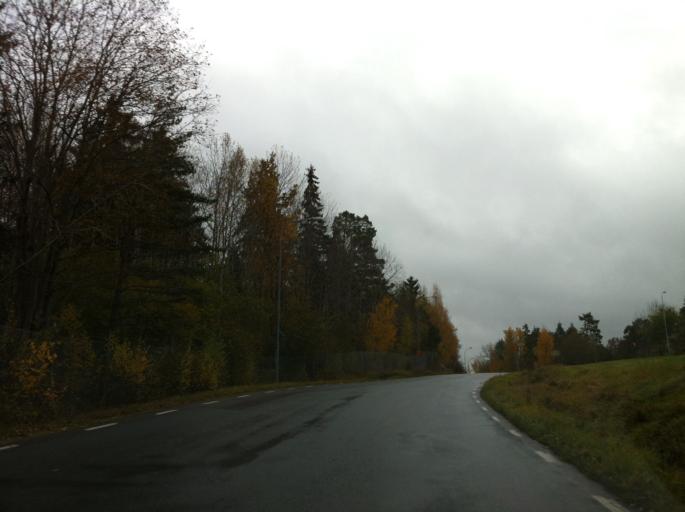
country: SE
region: Uppsala
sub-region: Osthammars Kommun
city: OEsthammar
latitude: 60.2690
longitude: 18.3662
